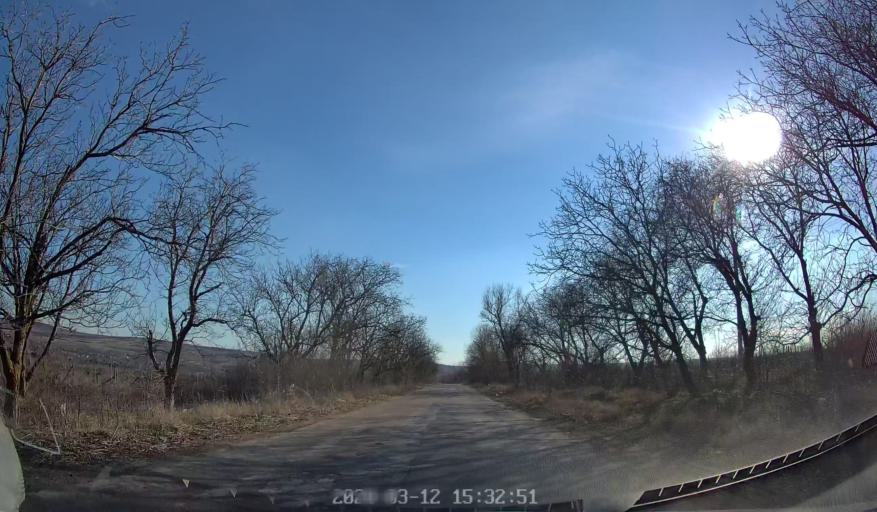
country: MD
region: Chisinau
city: Ciorescu
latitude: 47.1484
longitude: 28.9394
